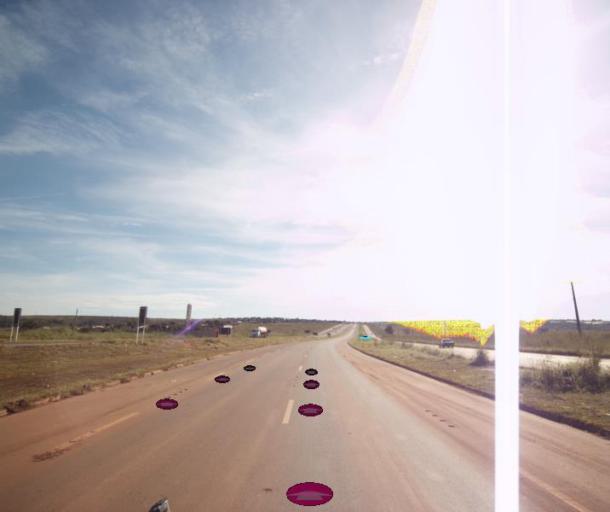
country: BR
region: Federal District
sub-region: Brasilia
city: Brasilia
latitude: -15.7513
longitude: -48.3247
